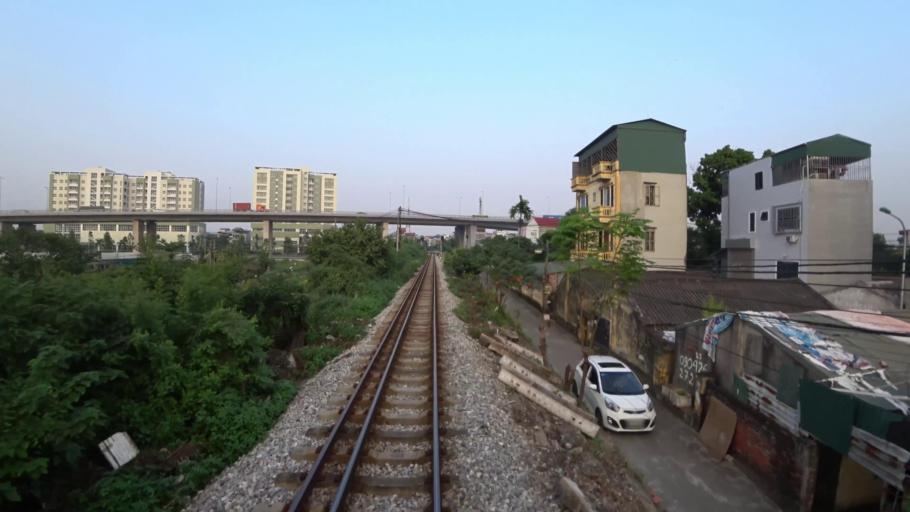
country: VN
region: Ha Noi
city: Trau Quy
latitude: 21.0723
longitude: 105.9034
